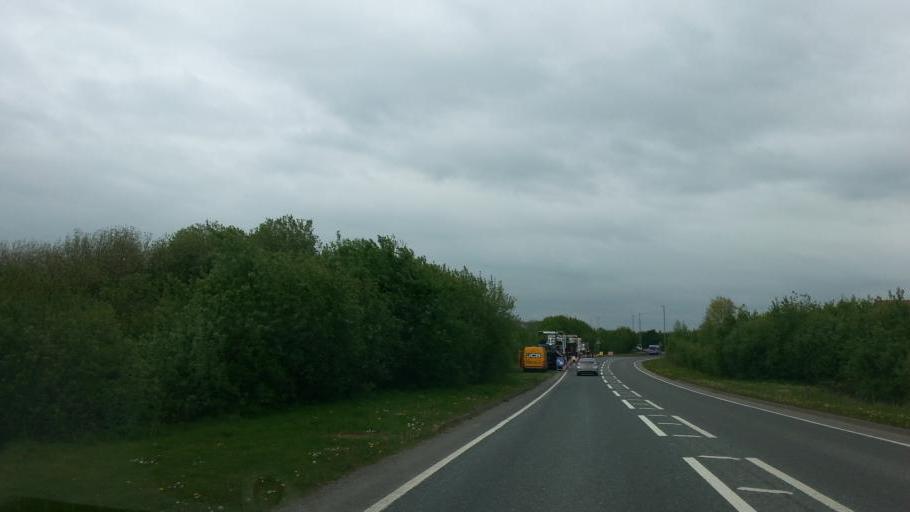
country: GB
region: England
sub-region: Lincolnshire
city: Bourne
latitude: 52.7635
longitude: -0.3957
